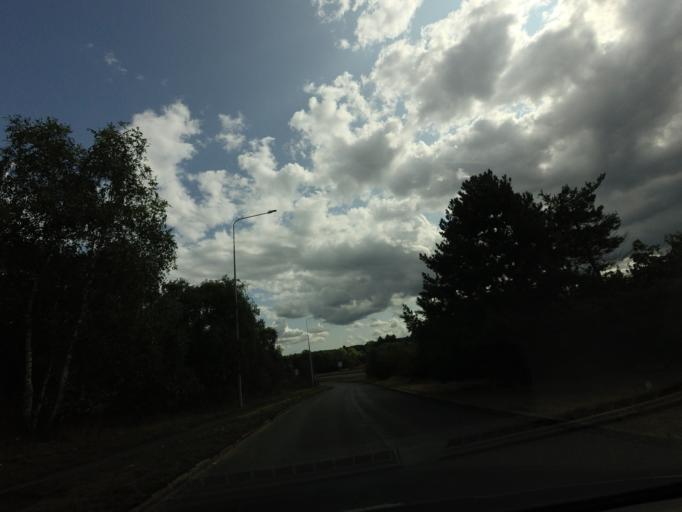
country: GB
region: England
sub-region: Kent
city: Harrietsham
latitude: 51.2612
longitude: 0.6134
